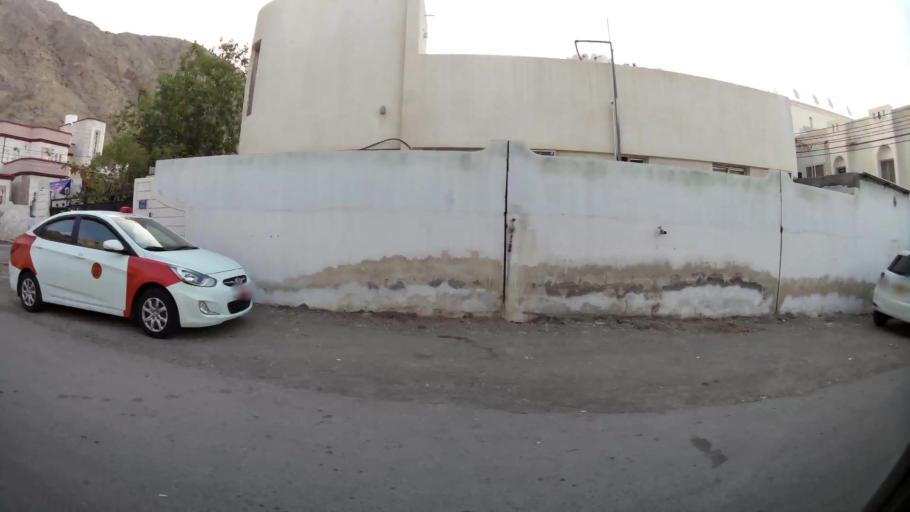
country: OM
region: Muhafazat Masqat
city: Muscat
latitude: 23.5676
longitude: 58.5705
